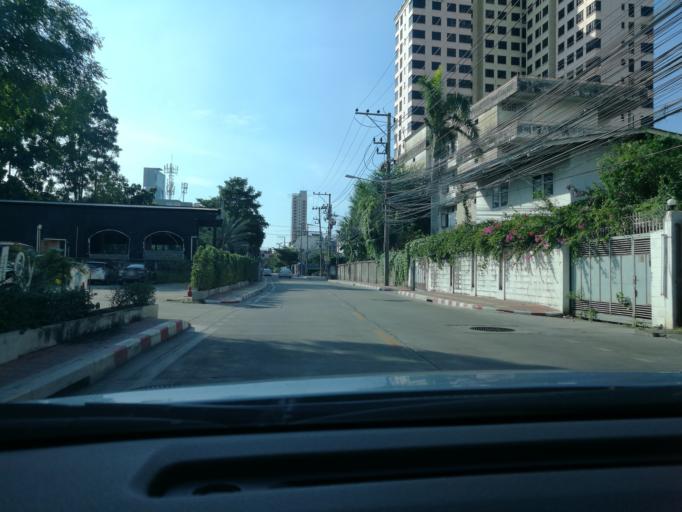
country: TH
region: Bangkok
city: Phaya Thai
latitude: 13.7878
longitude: 100.5436
